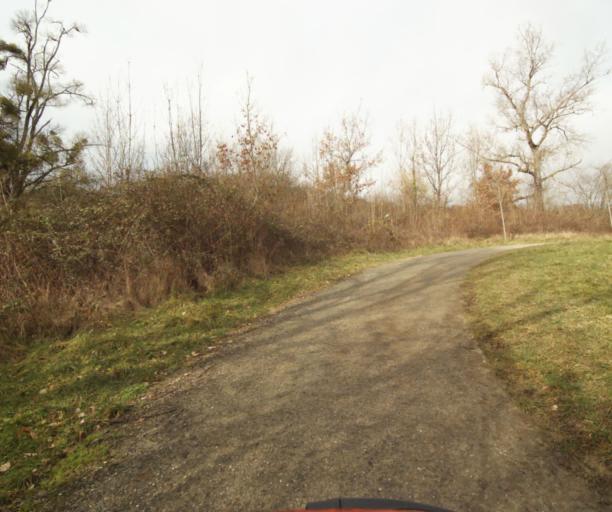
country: FR
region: Midi-Pyrenees
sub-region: Departement de l'Ariege
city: Pamiers
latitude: 43.1073
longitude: 1.6010
